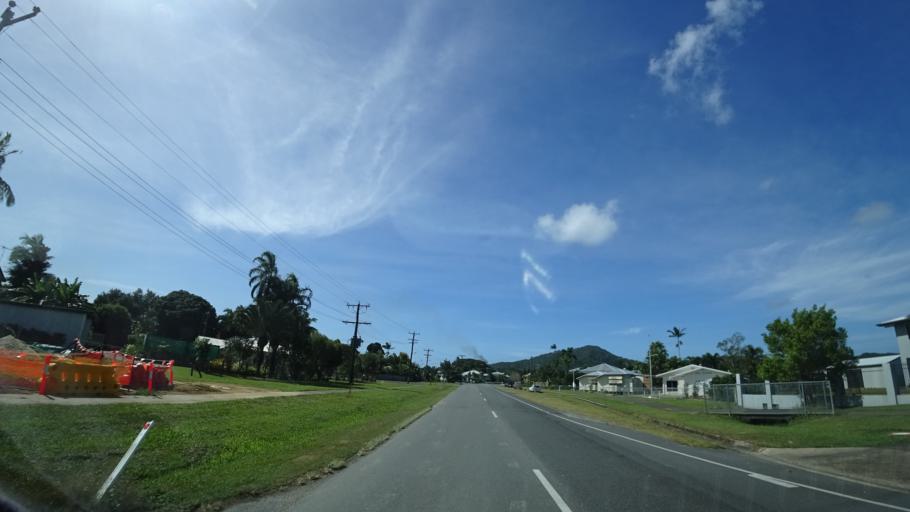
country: AU
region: Queensland
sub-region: Cairns
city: Port Douglas
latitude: -16.4644
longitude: 145.3692
